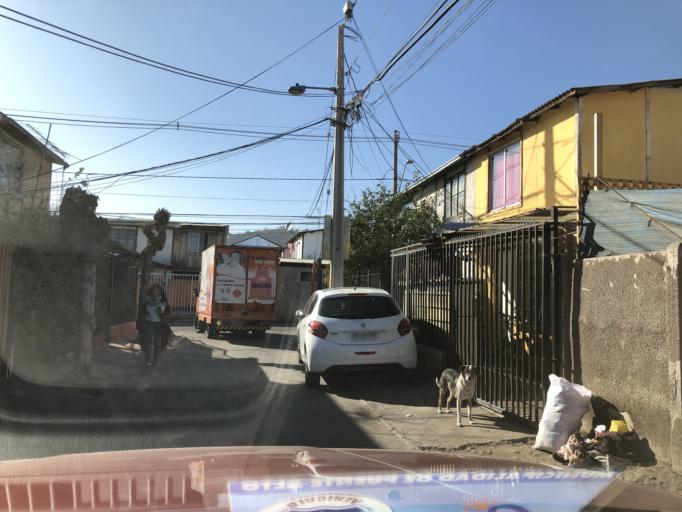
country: CL
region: Santiago Metropolitan
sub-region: Provincia de Cordillera
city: Puente Alto
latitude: -33.6003
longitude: -70.5620
